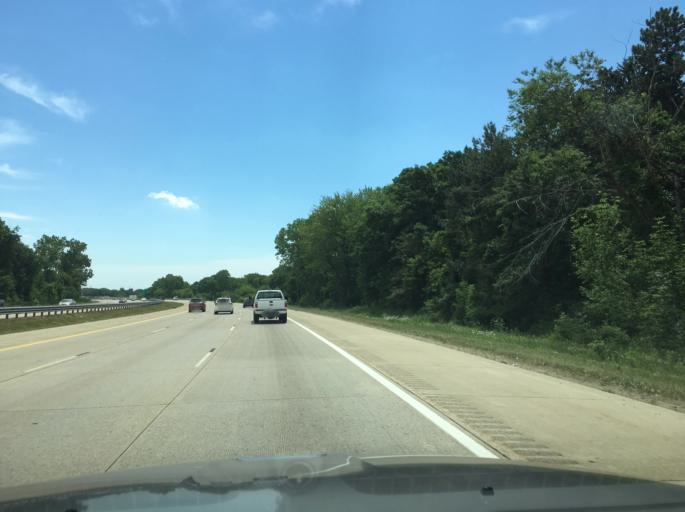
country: US
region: Michigan
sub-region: Oakland County
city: Rochester Hills
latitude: 42.6326
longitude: -83.1426
